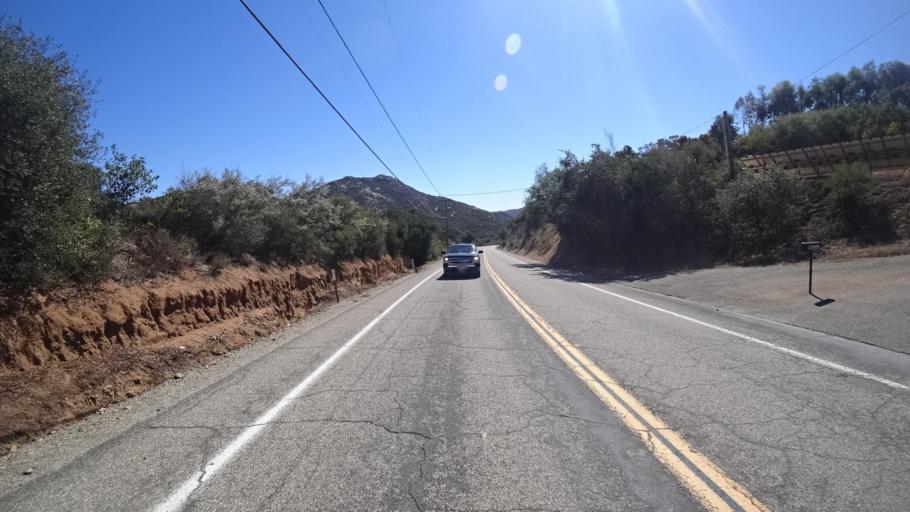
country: US
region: California
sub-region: San Diego County
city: Alpine
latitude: 32.7251
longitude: -116.7636
